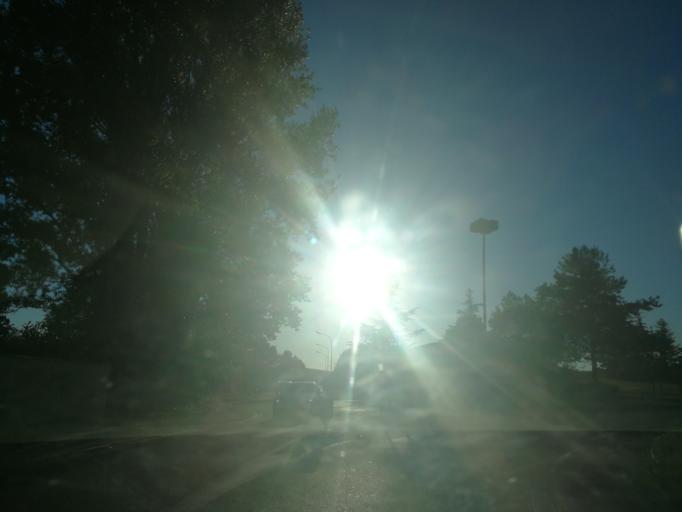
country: FR
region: Midi-Pyrenees
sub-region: Departement de la Haute-Garonne
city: Montrabe
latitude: 43.6497
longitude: 1.5118
